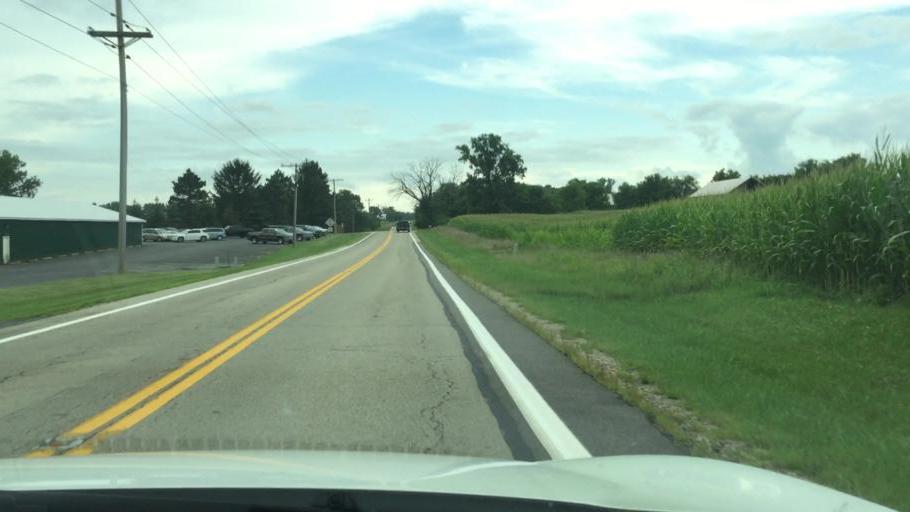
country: US
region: Ohio
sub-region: Champaign County
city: Mechanicsburg
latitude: 40.1056
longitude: -83.5334
